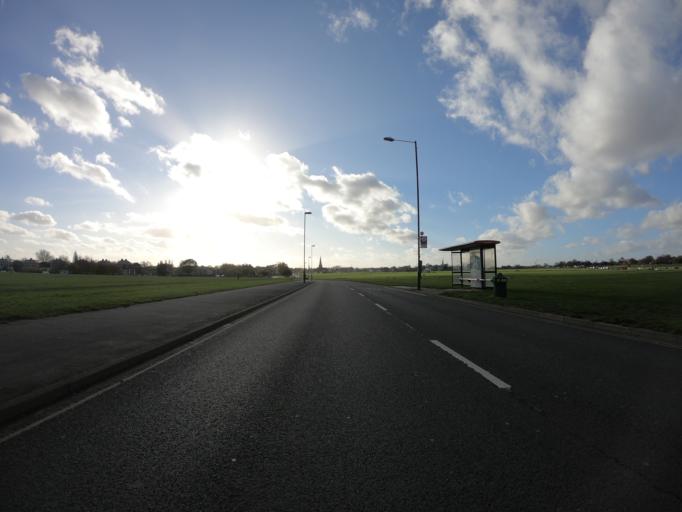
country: GB
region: England
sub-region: Greater London
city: Blackheath
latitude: 51.4724
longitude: 0.0140
